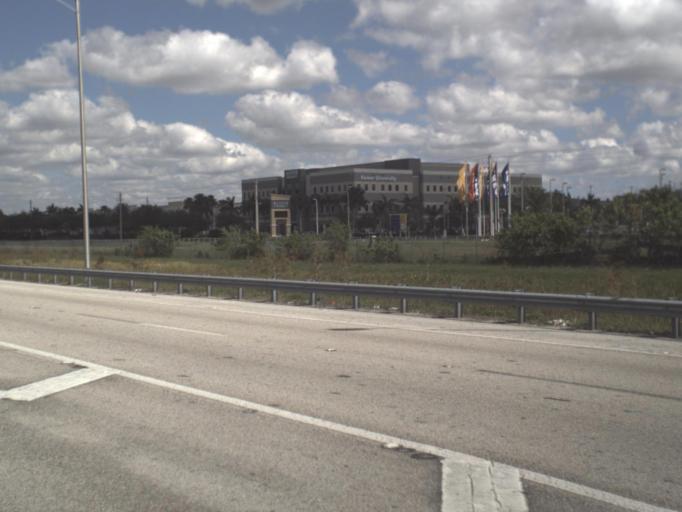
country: US
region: Florida
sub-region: Miami-Dade County
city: Sweetwater
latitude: 25.7918
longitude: -80.3858
